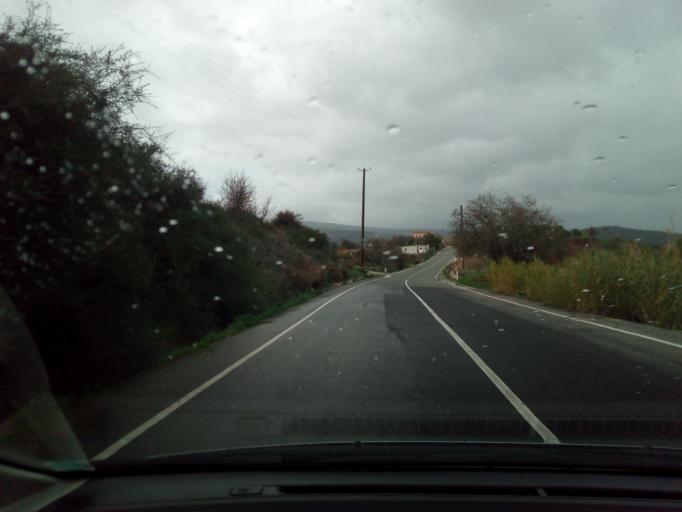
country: CY
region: Pafos
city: Polis
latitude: 34.9515
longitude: 32.4875
